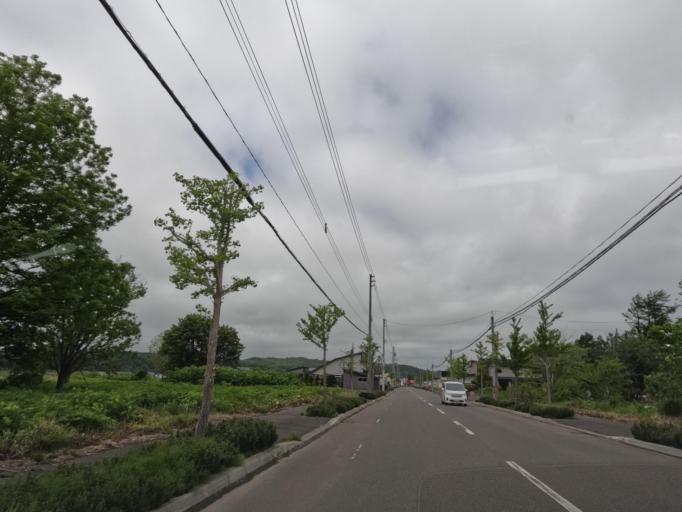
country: JP
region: Hokkaido
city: Tobetsu
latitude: 43.2345
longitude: 141.5147
